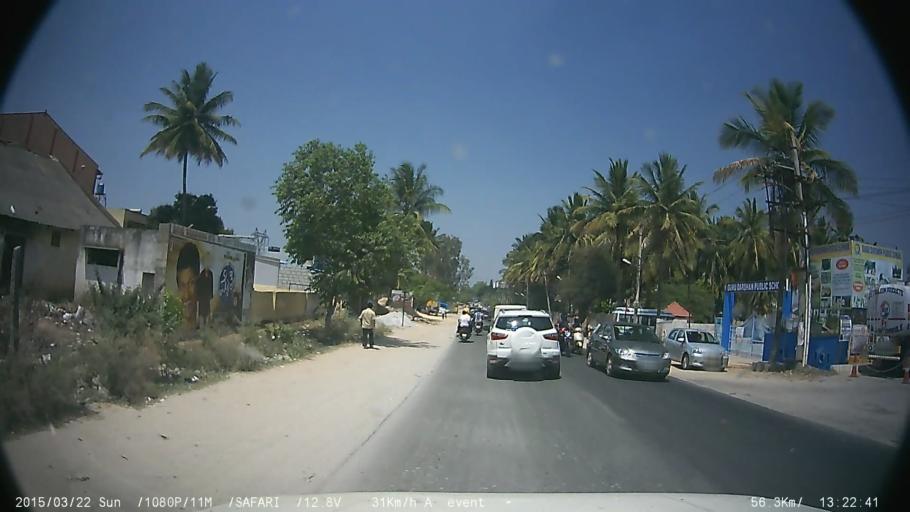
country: IN
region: Karnataka
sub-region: Bangalore Urban
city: Bangalore
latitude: 12.8595
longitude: 77.5895
